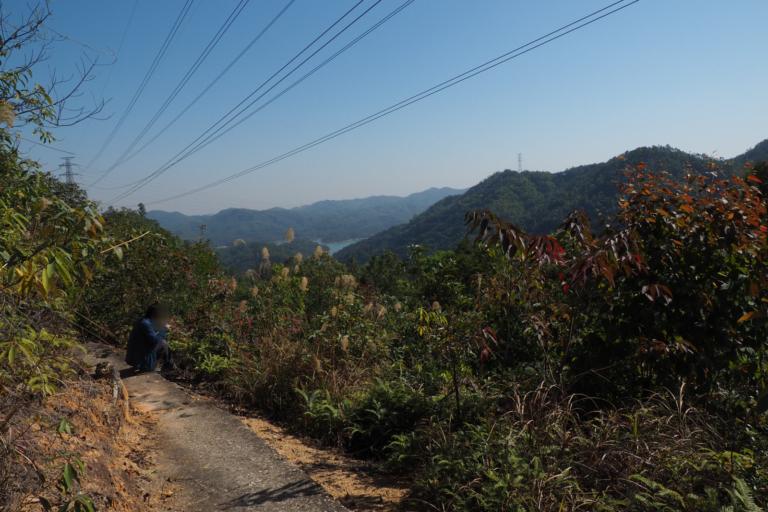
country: CN
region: Guangdong
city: Huancheng
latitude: 22.4677
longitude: 113.4113
